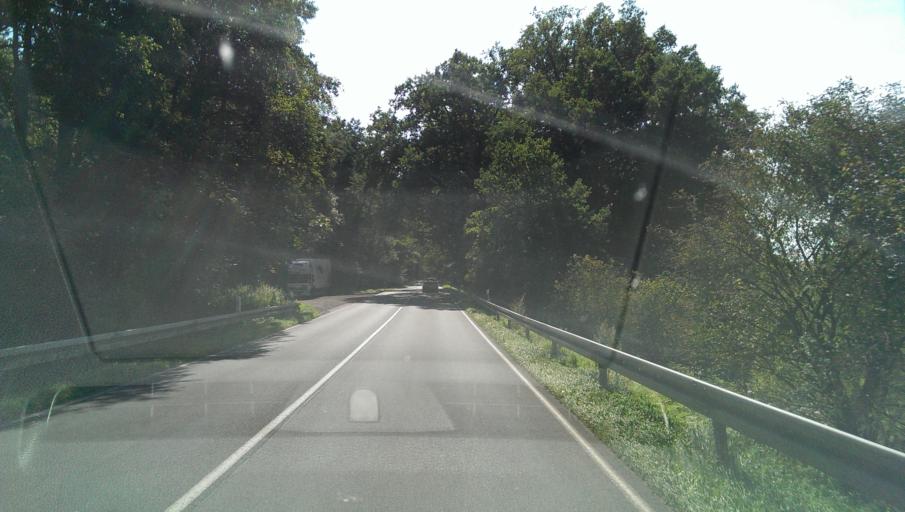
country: DE
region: Saxony-Anhalt
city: Kropstadt
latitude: 51.9397
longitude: 12.7190
